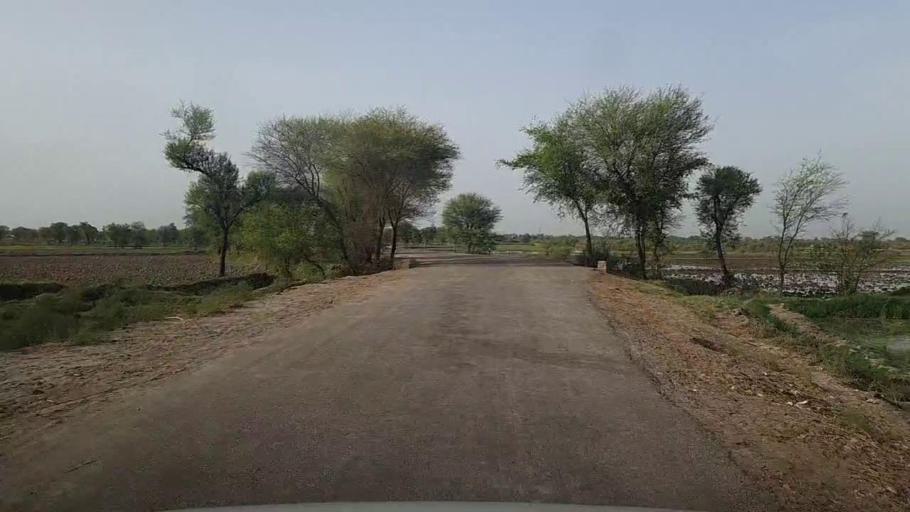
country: PK
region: Sindh
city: Khairpur Nathan Shah
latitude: 27.0909
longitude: 67.7943
